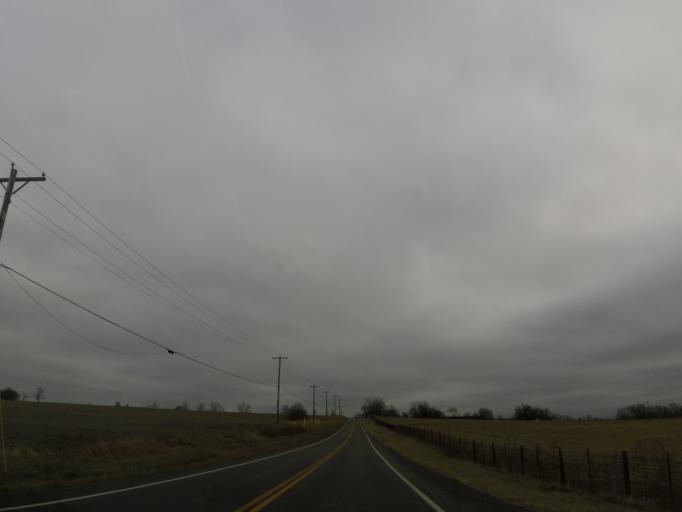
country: US
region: Kentucky
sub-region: Henry County
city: Eminence
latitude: 38.3616
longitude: -85.1216
